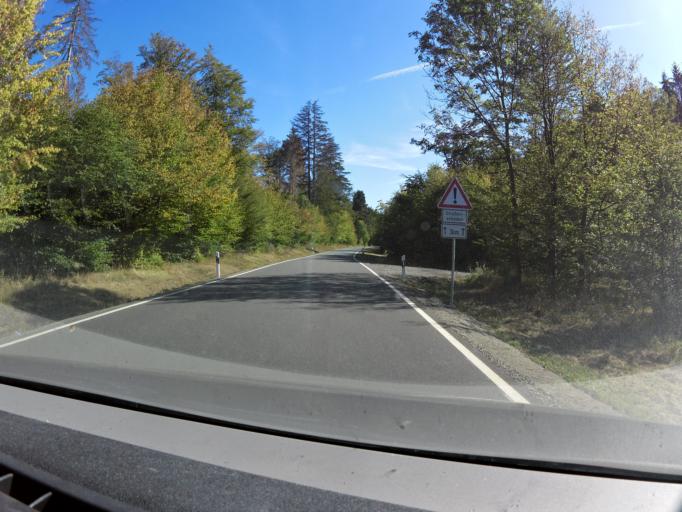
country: DE
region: Saxony-Anhalt
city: Hasselfelde
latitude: 51.6796
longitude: 10.9303
